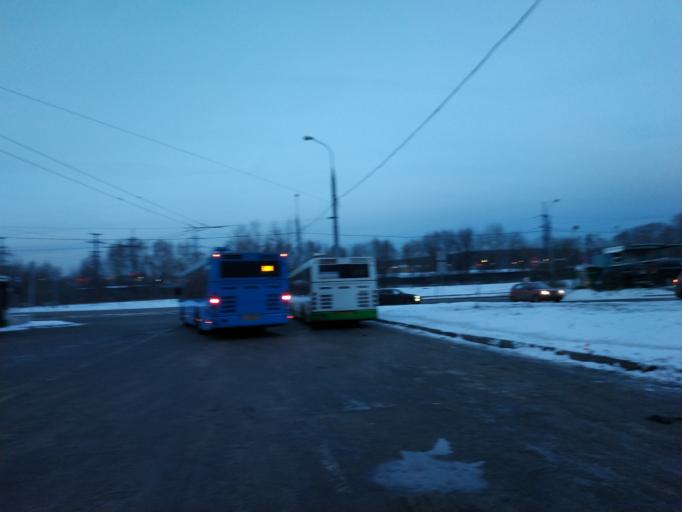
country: RU
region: Moscow
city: Lianozovo
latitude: 55.9053
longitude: 37.5903
